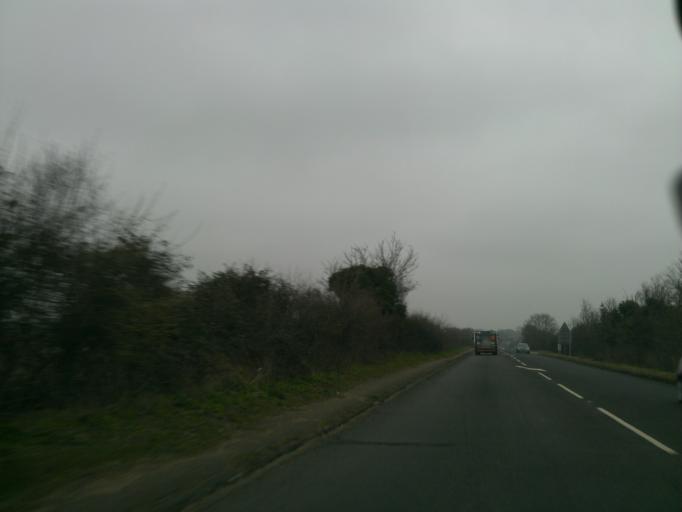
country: GB
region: England
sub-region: Essex
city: Alresford
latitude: 51.8751
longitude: 1.0085
